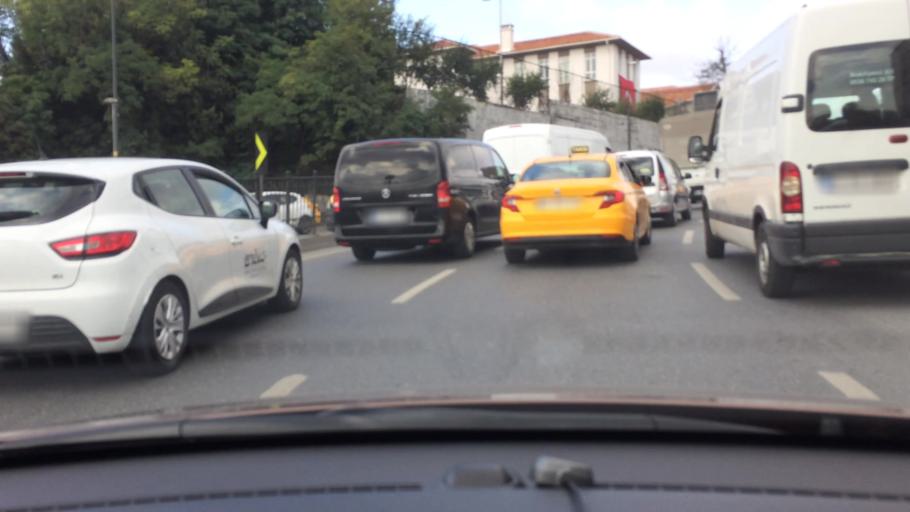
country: TR
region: Istanbul
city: Eminoenue
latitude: 41.0265
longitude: 28.9685
